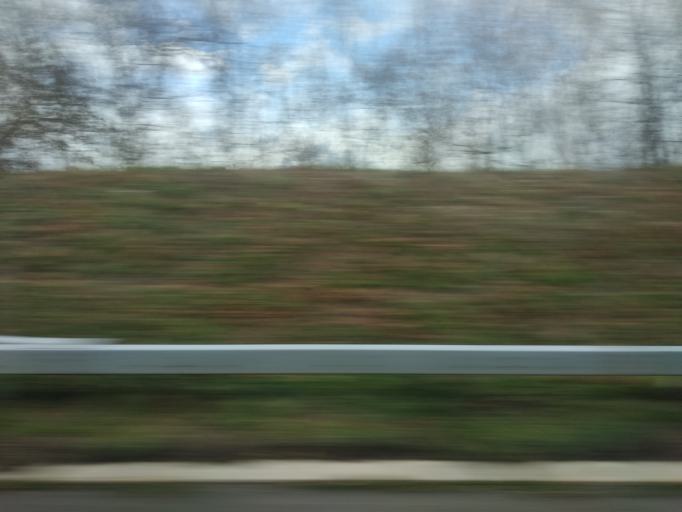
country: CH
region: Thurgau
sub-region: Muenchwilen District
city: Munchwilen
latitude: 47.4723
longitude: 8.9892
